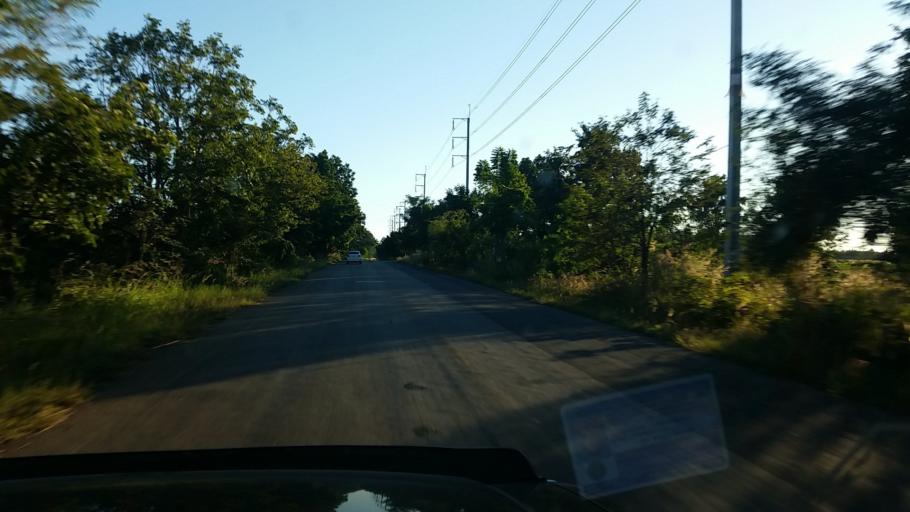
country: TH
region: Chaiyaphum
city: Sap Yai
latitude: 15.6730
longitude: 101.6749
